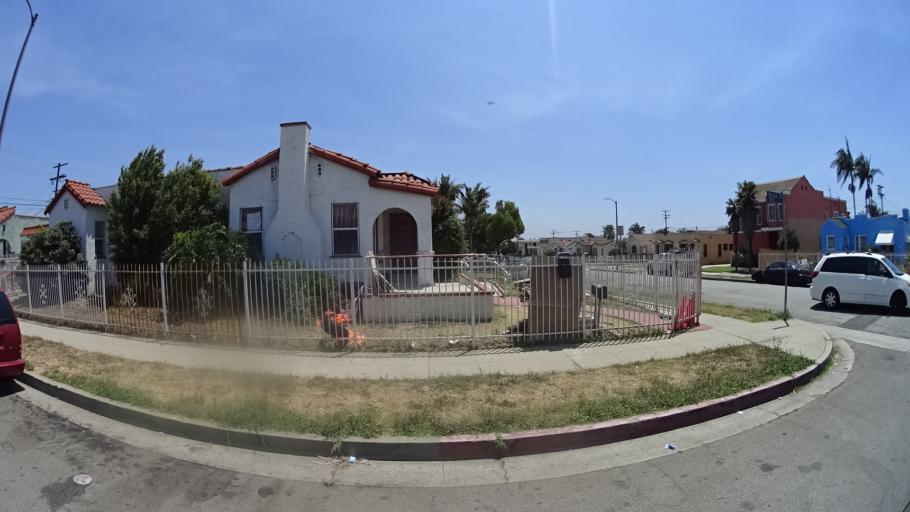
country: US
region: California
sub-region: Los Angeles County
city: Westmont
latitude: 33.9656
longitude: -118.3068
